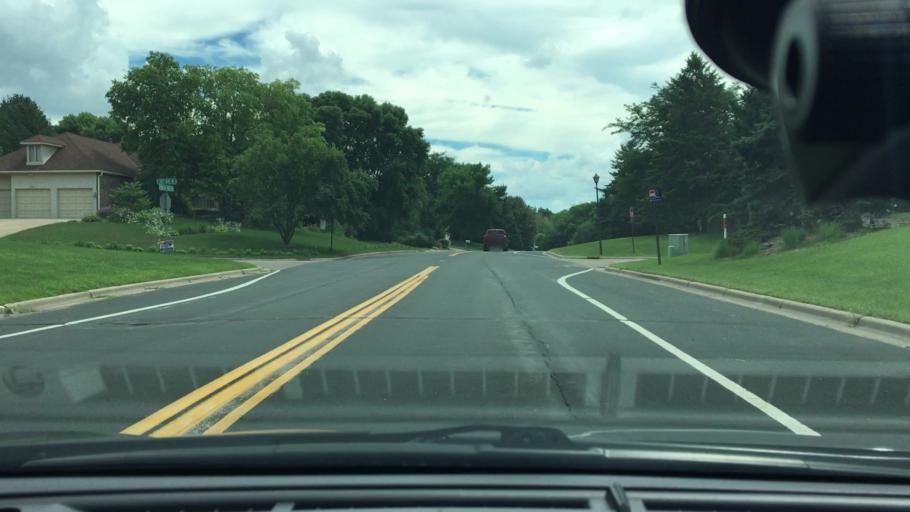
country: US
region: Minnesota
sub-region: Hennepin County
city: New Hope
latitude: 45.0109
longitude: -93.4123
